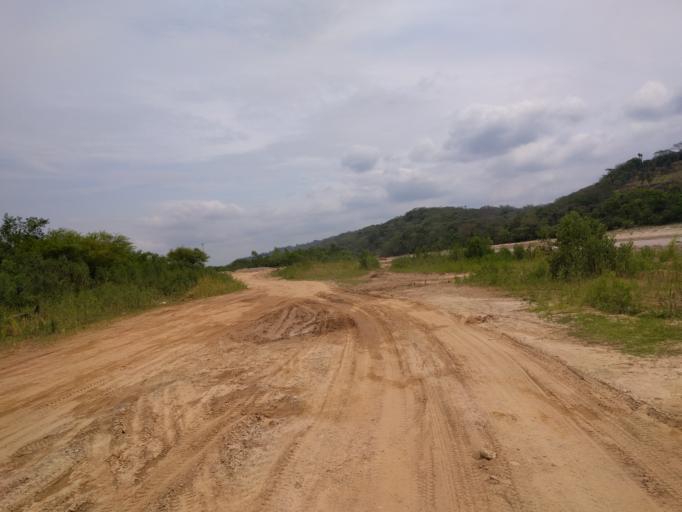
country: BO
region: Santa Cruz
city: Santa Rita
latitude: -17.9378
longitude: -63.3628
